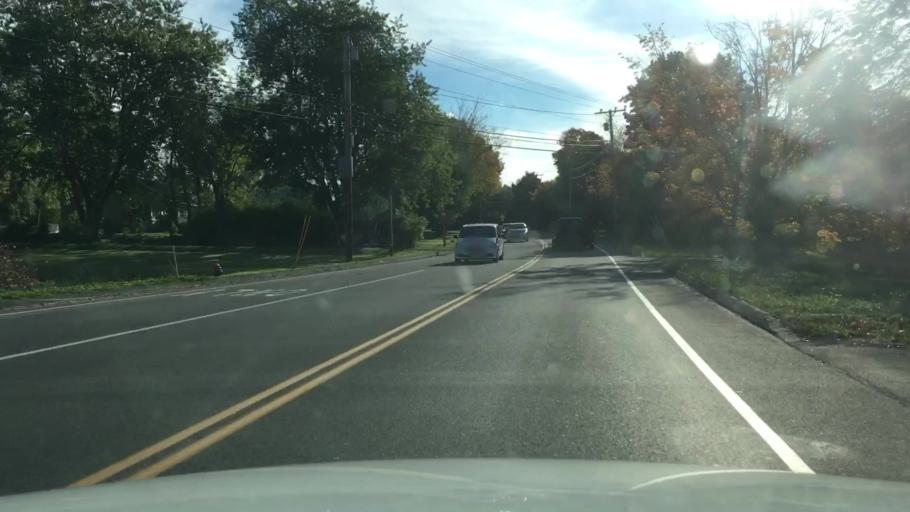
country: US
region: Maine
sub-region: Knox County
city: Thomaston
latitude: 44.0769
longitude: -69.2033
